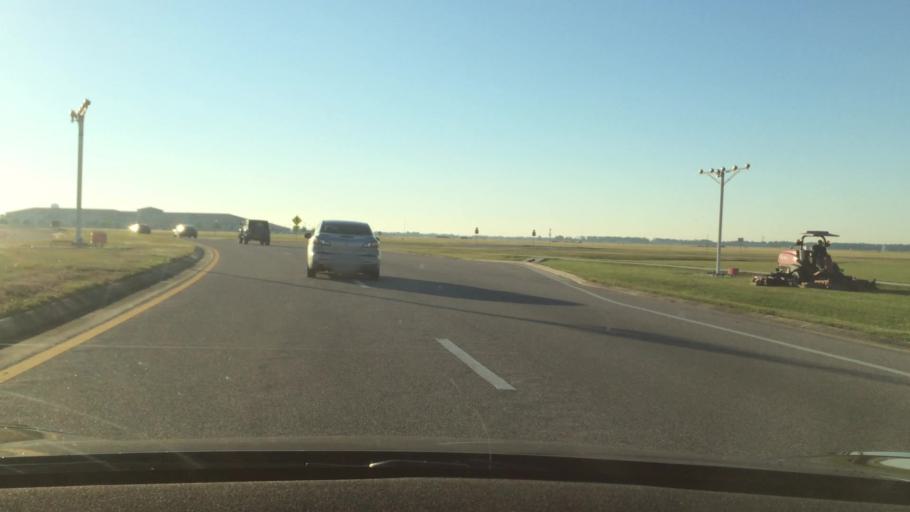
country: US
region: Florida
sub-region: Hillsborough County
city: Tampa
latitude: 27.8655
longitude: -82.5061
